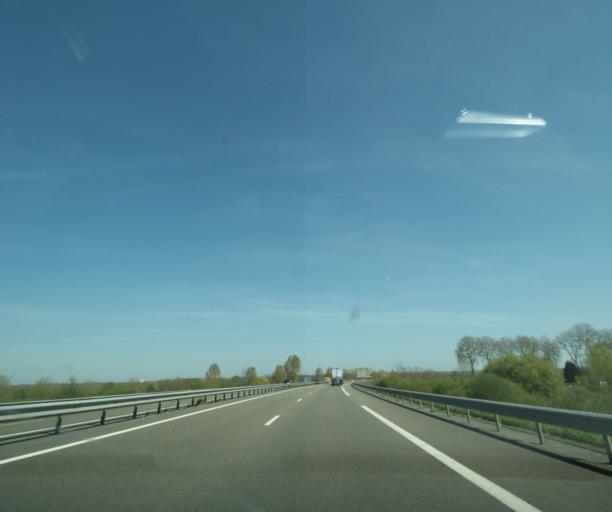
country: FR
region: Bourgogne
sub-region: Departement de la Nievre
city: Sermoise-sur-Loire
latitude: 46.9637
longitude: 3.1786
